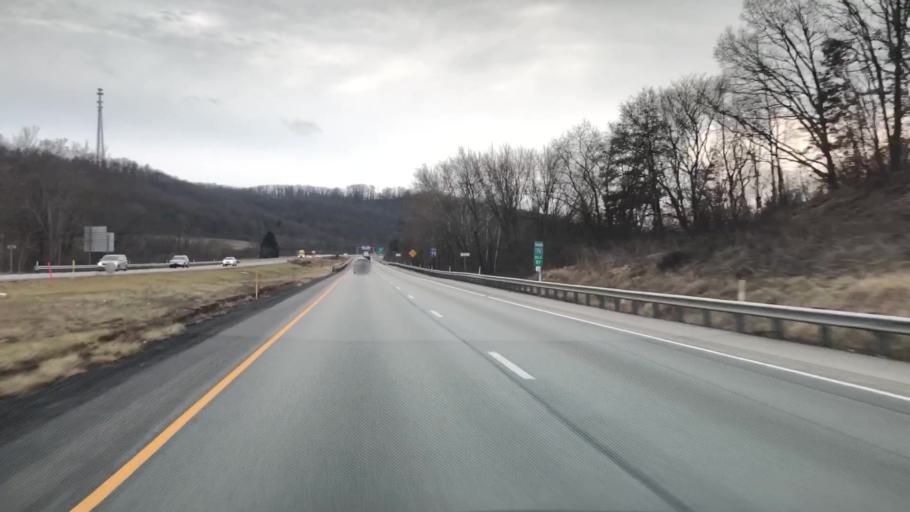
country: US
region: Pennsylvania
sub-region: Butler County
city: Zelienople
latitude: 40.8051
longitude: -80.1178
